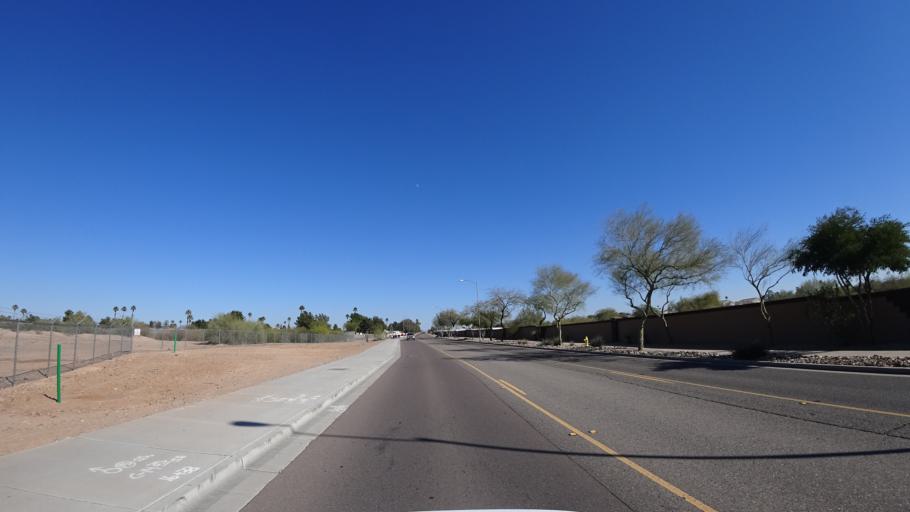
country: US
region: Arizona
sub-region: Maricopa County
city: Surprise
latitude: 33.6525
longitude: -112.3002
